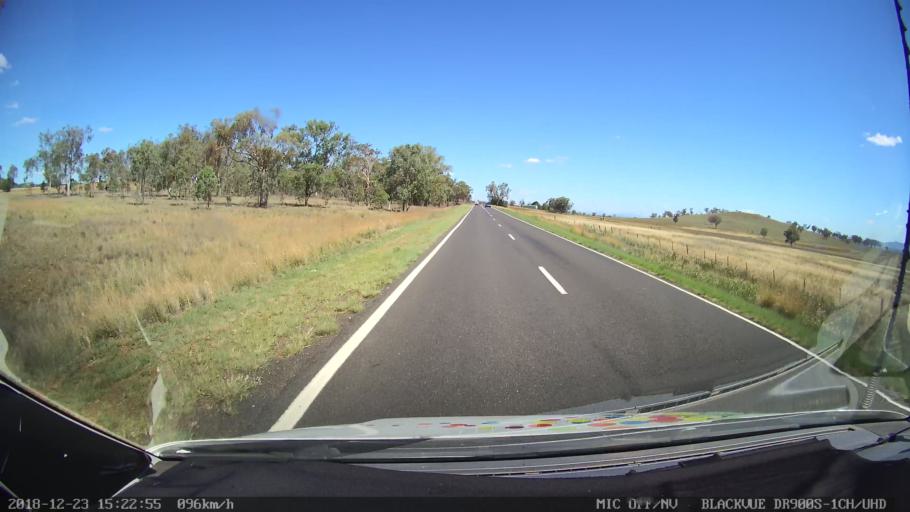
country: AU
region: New South Wales
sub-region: Tamworth Municipality
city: Manilla
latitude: -30.8739
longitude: 150.8095
